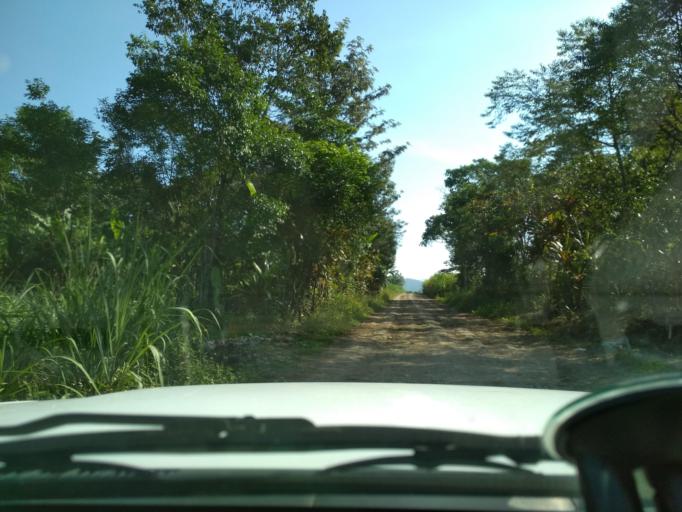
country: MX
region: Veracruz
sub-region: Chocaman
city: San Jose Neria
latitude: 18.9869
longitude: -97.0054
